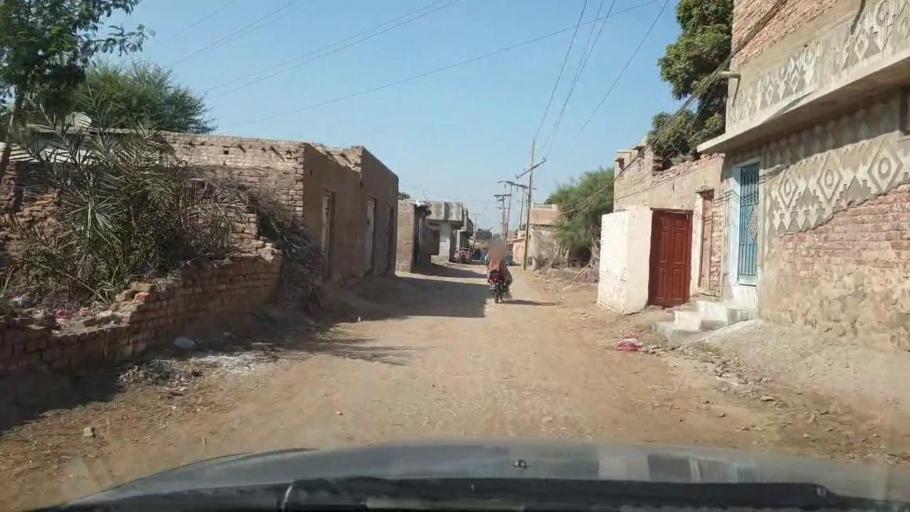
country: PK
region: Sindh
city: Tando Muhammad Khan
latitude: 25.1322
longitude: 68.5482
